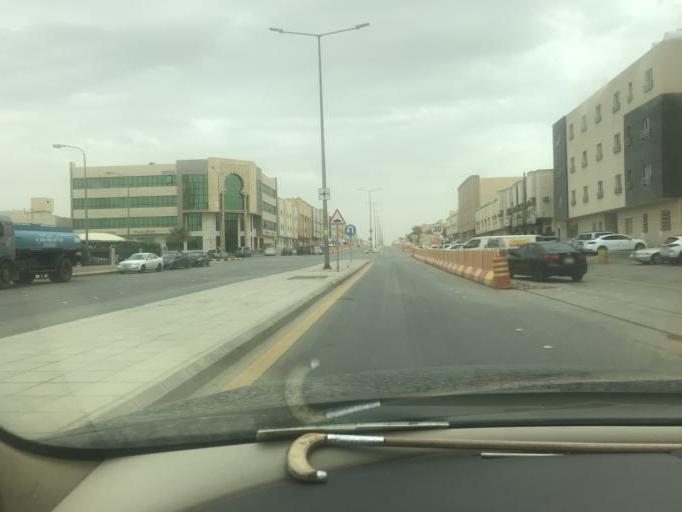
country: SA
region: Ar Riyad
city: Riyadh
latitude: 24.7960
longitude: 46.7083
